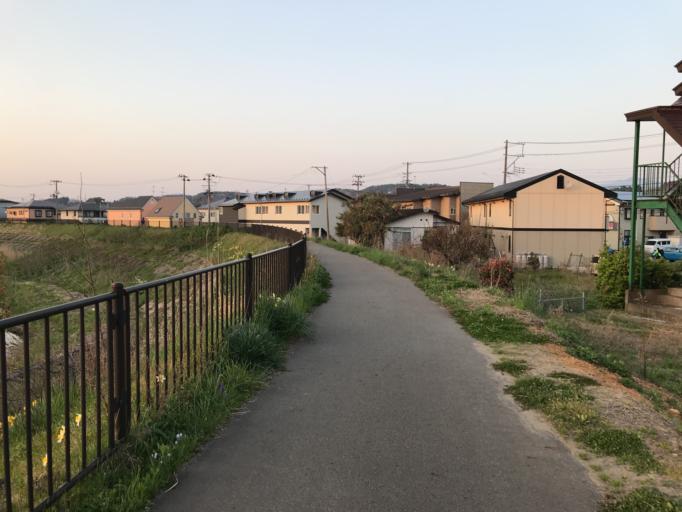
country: JP
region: Akita
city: Akita
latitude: 39.7291
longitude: 140.1276
